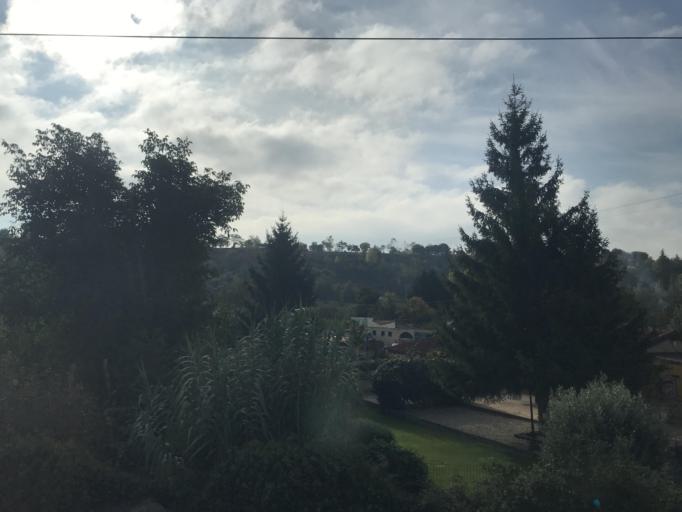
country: ES
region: Castille and Leon
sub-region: Provincia de Burgos
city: Miranda de Ebro
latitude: 42.6842
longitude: -2.9590
